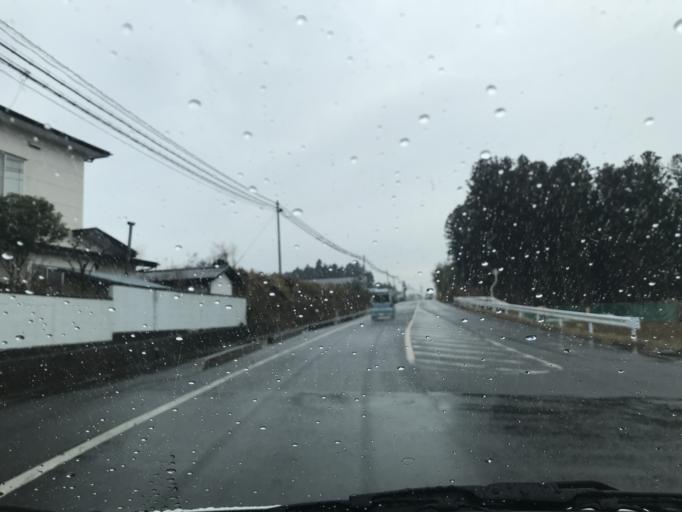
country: JP
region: Miyagi
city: Wakuya
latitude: 38.6923
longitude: 141.1705
